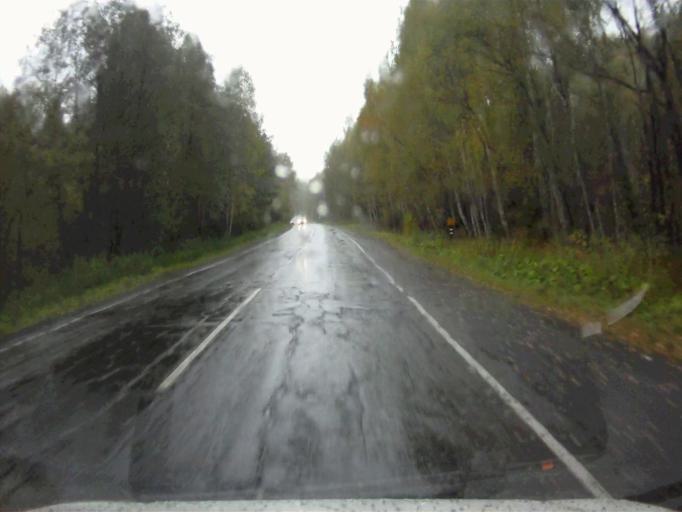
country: RU
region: Chelyabinsk
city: Kyshtym
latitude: 55.9089
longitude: 60.4375
